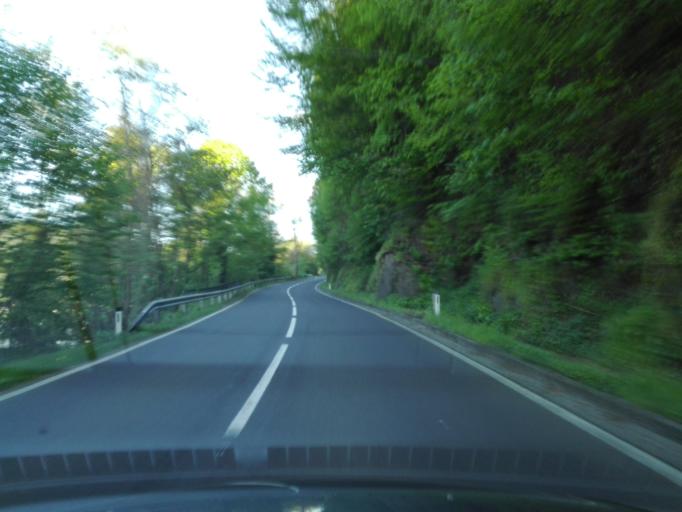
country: AT
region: Upper Austria
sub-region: Politischer Bezirk Rohrbach
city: Pfarrkirchen im Muehlkreis
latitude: 48.4672
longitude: 13.7783
